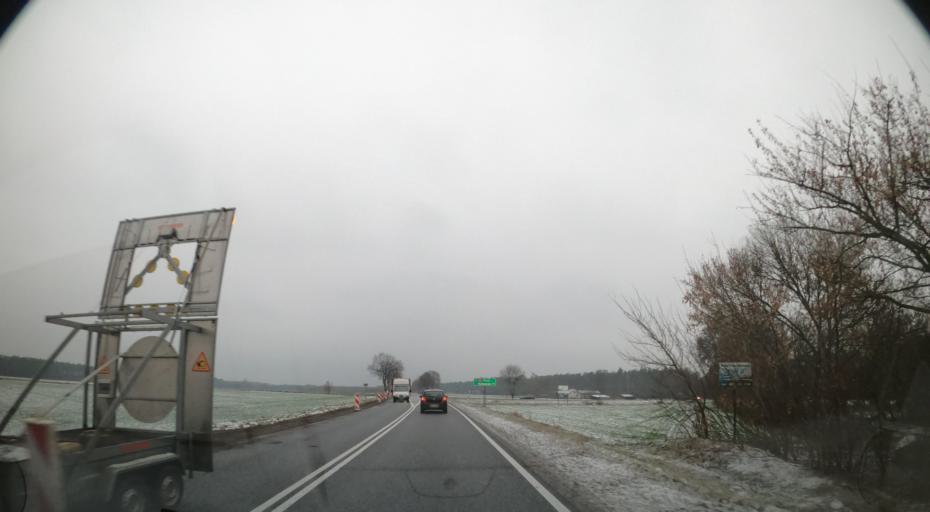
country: PL
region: Masovian Voivodeship
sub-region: Powiat plocki
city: Mala Wies
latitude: 52.4098
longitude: 20.1325
